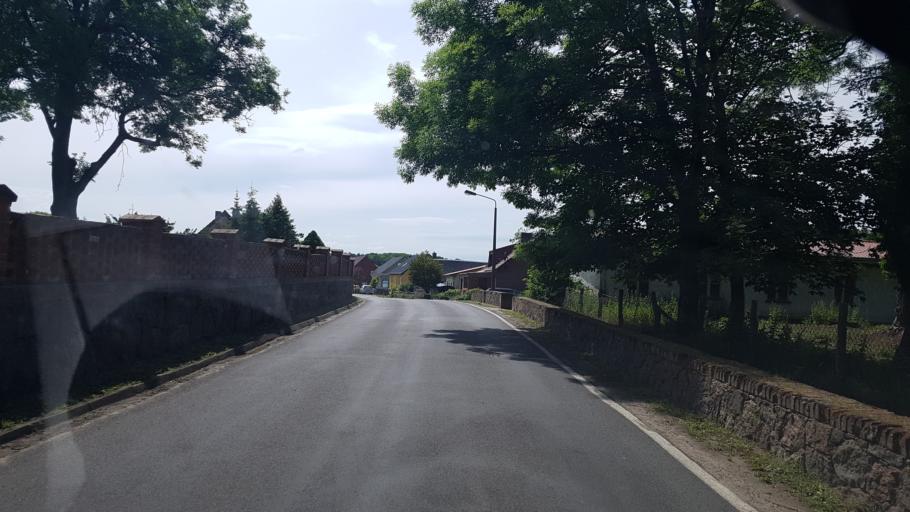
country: DE
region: Mecklenburg-Vorpommern
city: Strasburg
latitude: 53.4144
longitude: 13.7668
